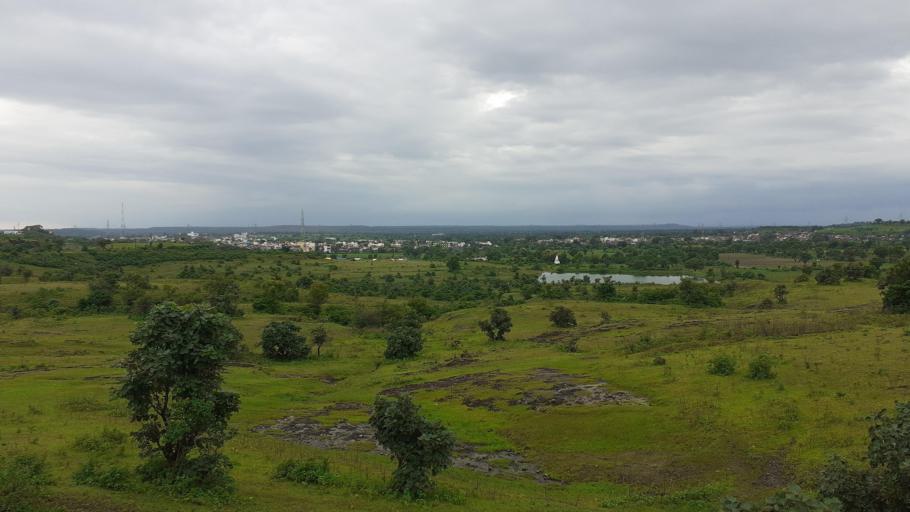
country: IN
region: Maharashtra
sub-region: Nagpur Division
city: Katol
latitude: 21.1613
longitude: 78.4238
